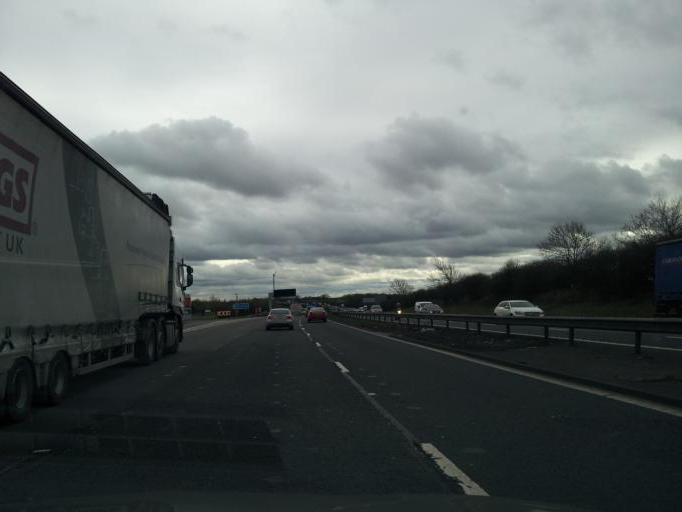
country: GB
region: England
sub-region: Staffordshire
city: Stone
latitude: 52.8759
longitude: -2.1646
